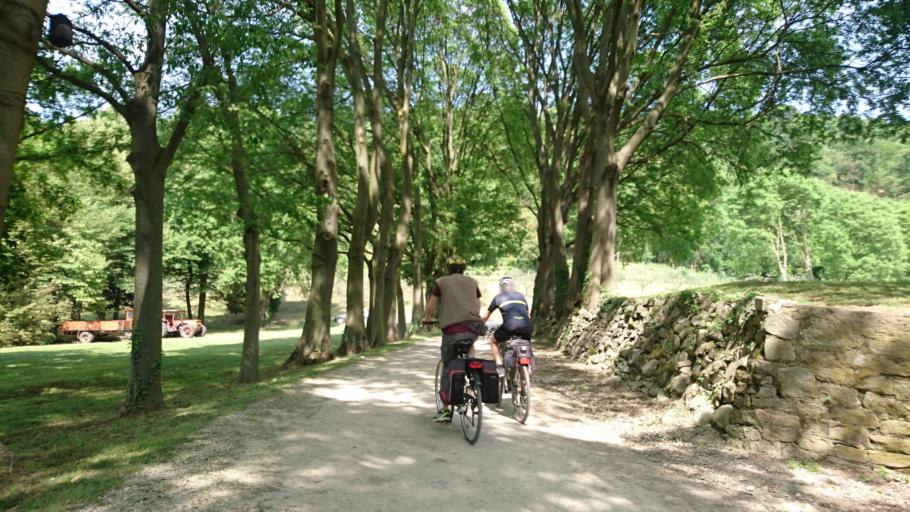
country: IT
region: Veneto
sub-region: Provincia di Padova
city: Battaglia Terme
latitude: 45.2822
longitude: 11.7622
